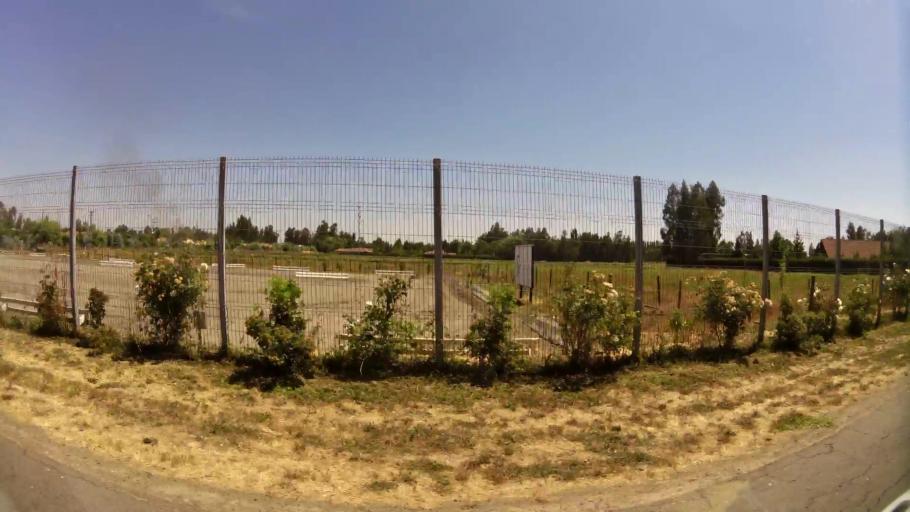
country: CL
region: Maule
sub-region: Provincia de Curico
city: Curico
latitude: -35.0006
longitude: -71.2098
